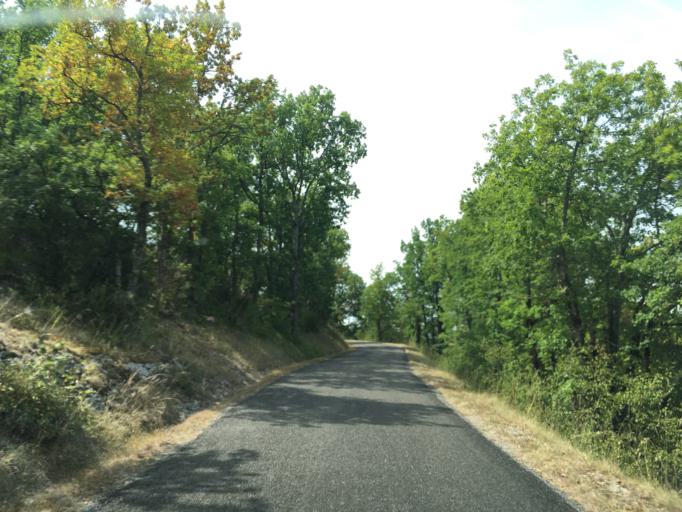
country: FR
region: Midi-Pyrenees
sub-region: Departement du Lot
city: Le Vigan
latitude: 44.7609
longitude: 1.5516
